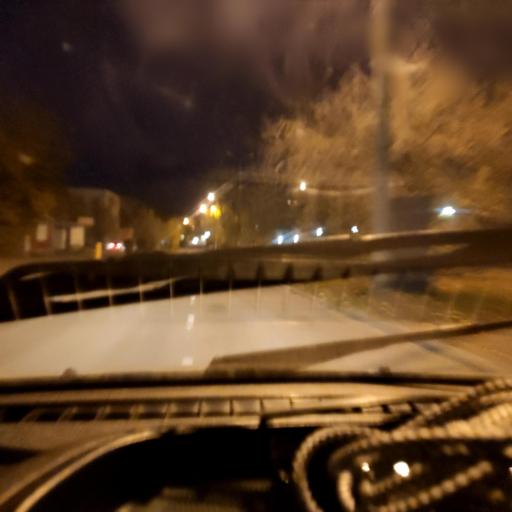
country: RU
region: Samara
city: Zhigulevsk
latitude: 53.4706
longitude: 49.5312
